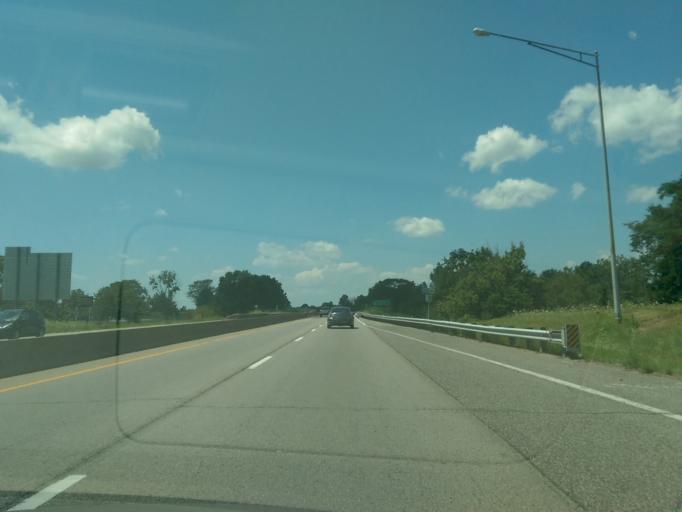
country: US
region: Missouri
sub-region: Boone County
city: Columbia
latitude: 38.9693
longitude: -92.3368
